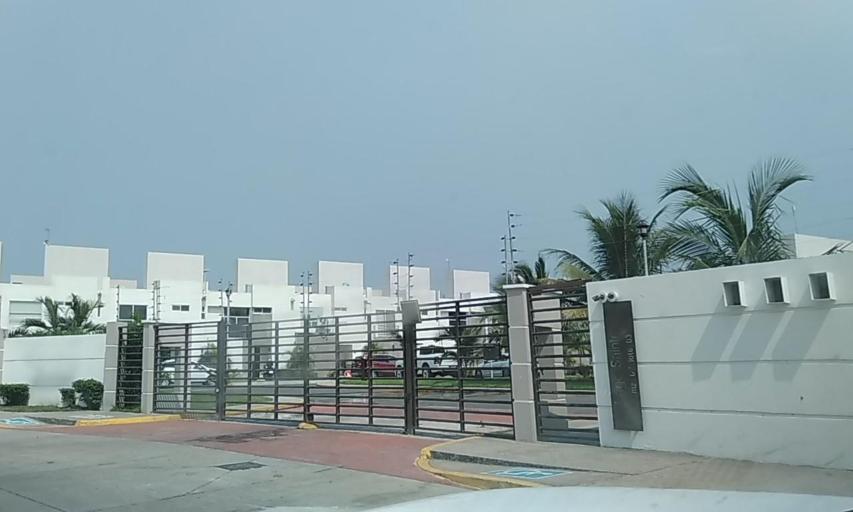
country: MX
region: Veracruz
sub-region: Veracruz
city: Hacienda Sotavento
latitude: 19.1333
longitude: -96.1716
